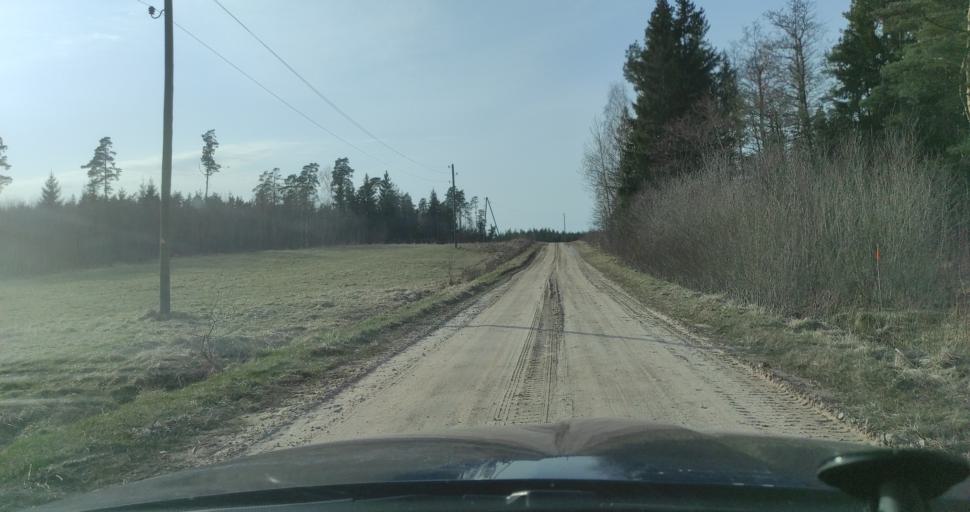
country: LV
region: Kuldigas Rajons
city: Kuldiga
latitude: 57.0122
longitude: 22.0169
